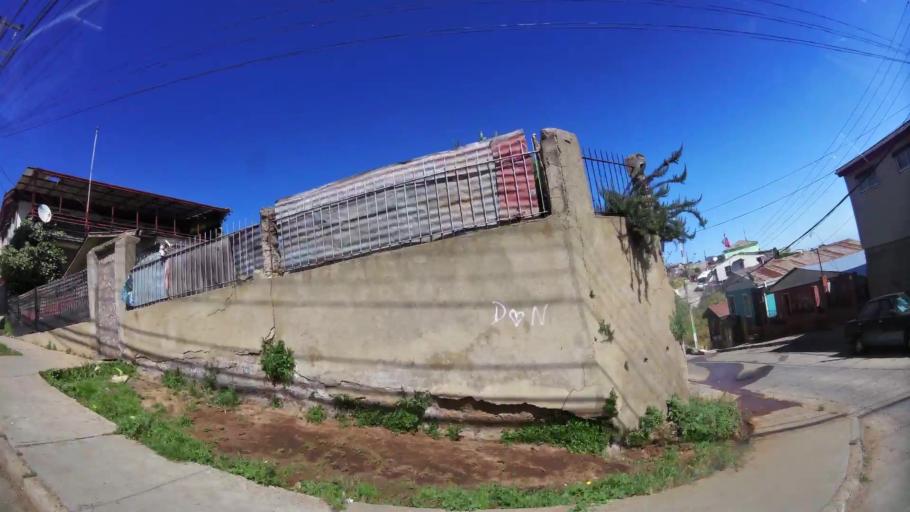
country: CL
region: Valparaiso
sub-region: Provincia de Valparaiso
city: Valparaiso
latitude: -33.0514
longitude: -71.6449
